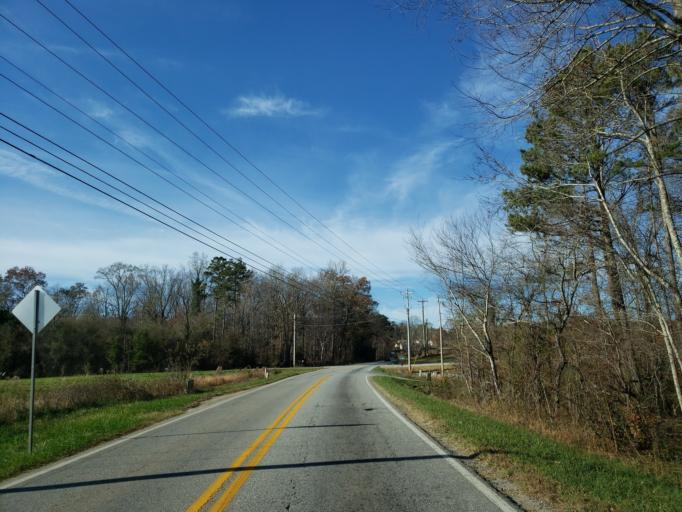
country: US
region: Georgia
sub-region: Lumpkin County
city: Dahlonega
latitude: 34.4460
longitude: -83.9892
